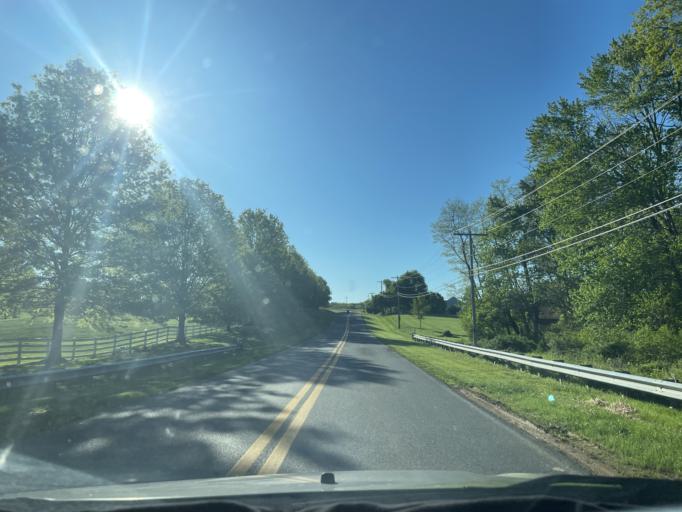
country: US
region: Maryland
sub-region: Carroll County
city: Mount Airy
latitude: 39.4058
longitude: -77.1218
